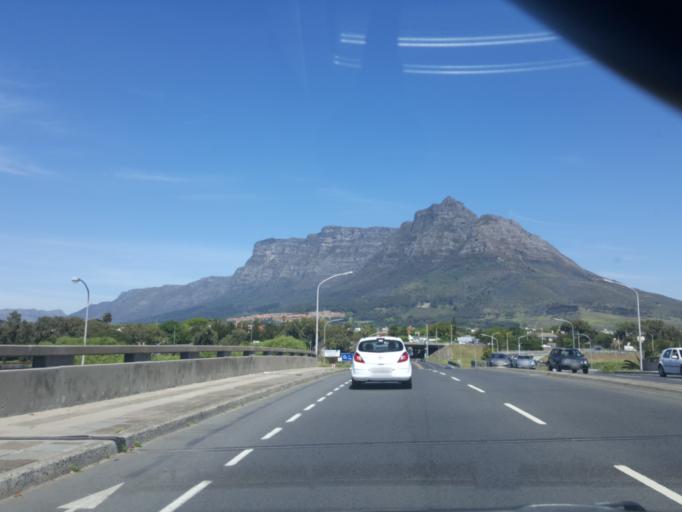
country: ZA
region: Western Cape
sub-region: City of Cape Town
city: Rosebank
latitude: -33.9463
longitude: 18.4888
